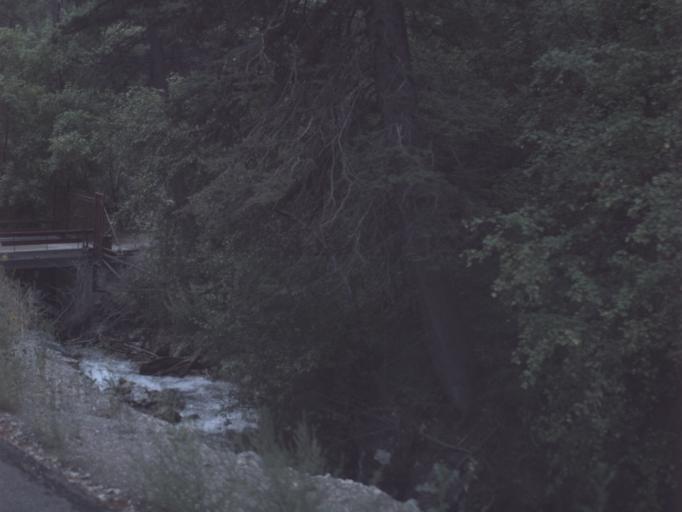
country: US
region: Utah
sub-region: Utah County
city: Orem
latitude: 40.3863
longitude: -111.5737
